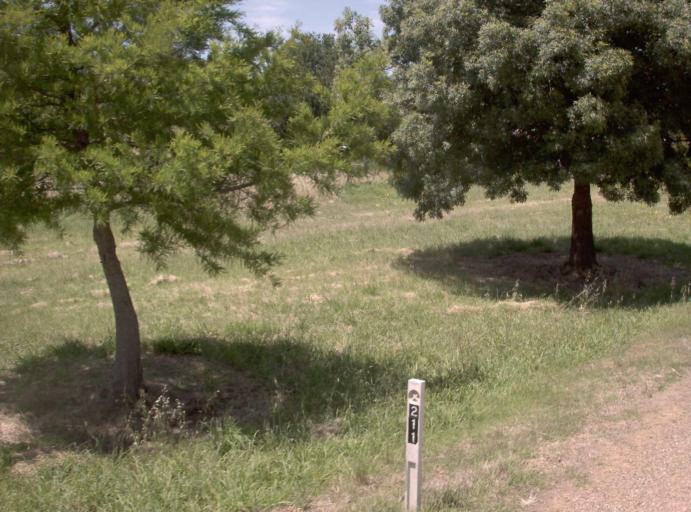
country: AU
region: Victoria
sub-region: East Gippsland
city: Bairnsdale
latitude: -37.2536
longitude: 147.7116
